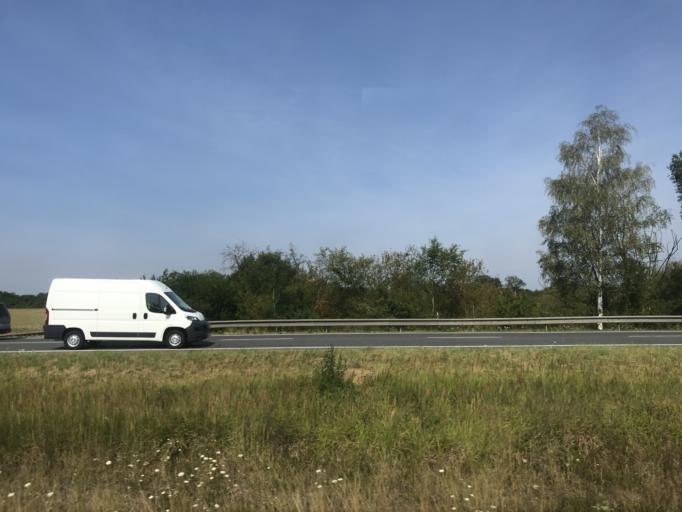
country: CZ
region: Central Bohemia
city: Bystrice
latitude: 49.7378
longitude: 14.6621
